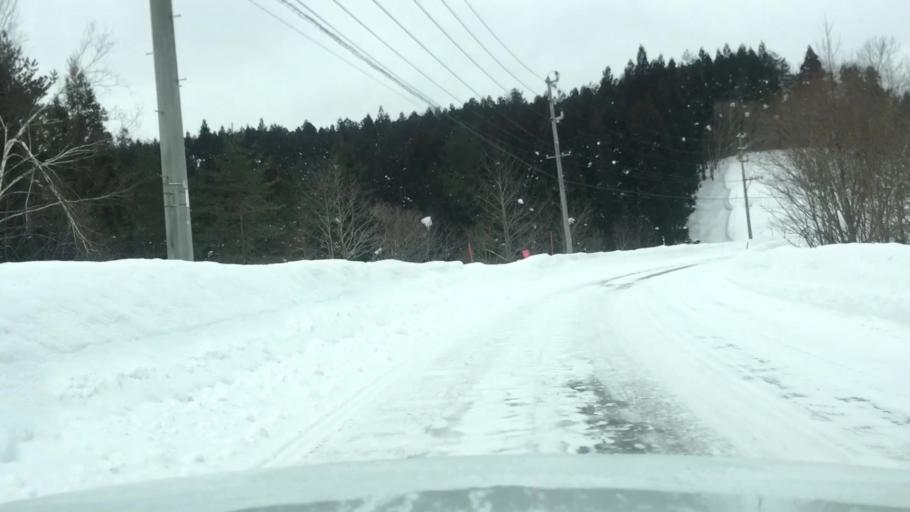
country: JP
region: Akita
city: Hanawa
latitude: 39.9951
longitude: 140.9921
